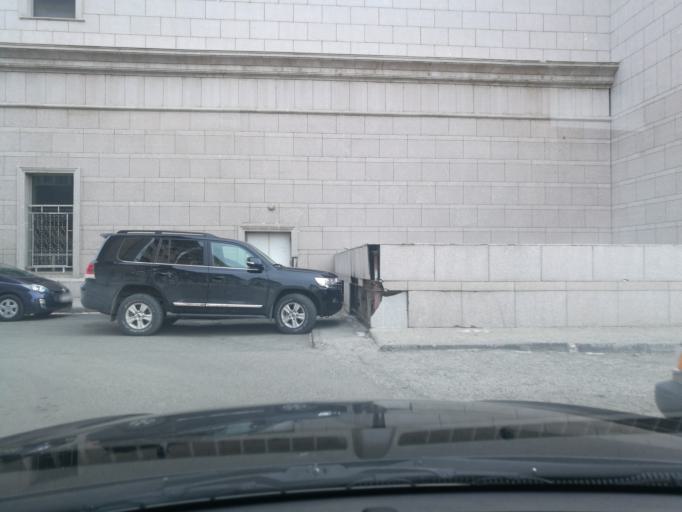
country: MN
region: Ulaanbaatar
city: Ulaanbaatar
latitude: 47.9153
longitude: 106.9010
